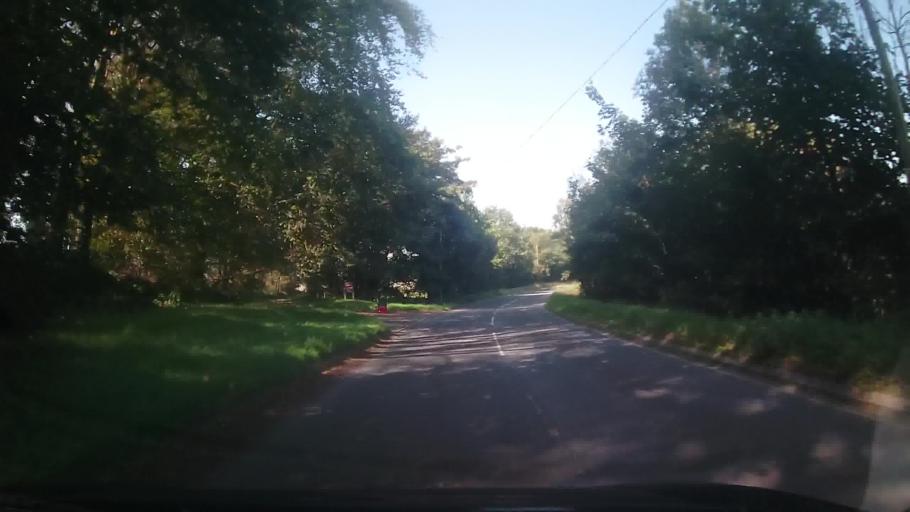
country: GB
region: Wales
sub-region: Pembrokeshire
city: Camrose
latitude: 51.8529
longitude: -5.0123
